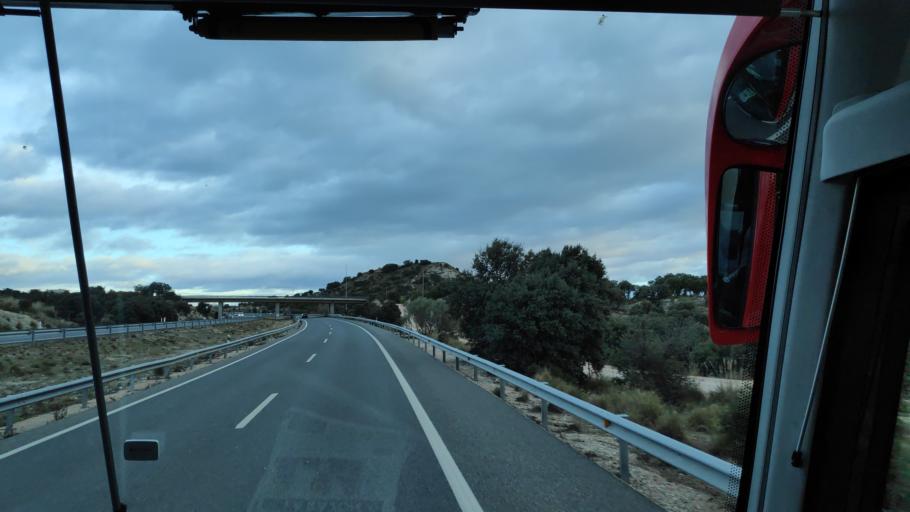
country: ES
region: Madrid
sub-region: Provincia de Madrid
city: Fuentiduena de Tajo
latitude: 40.1423
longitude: -3.2103
